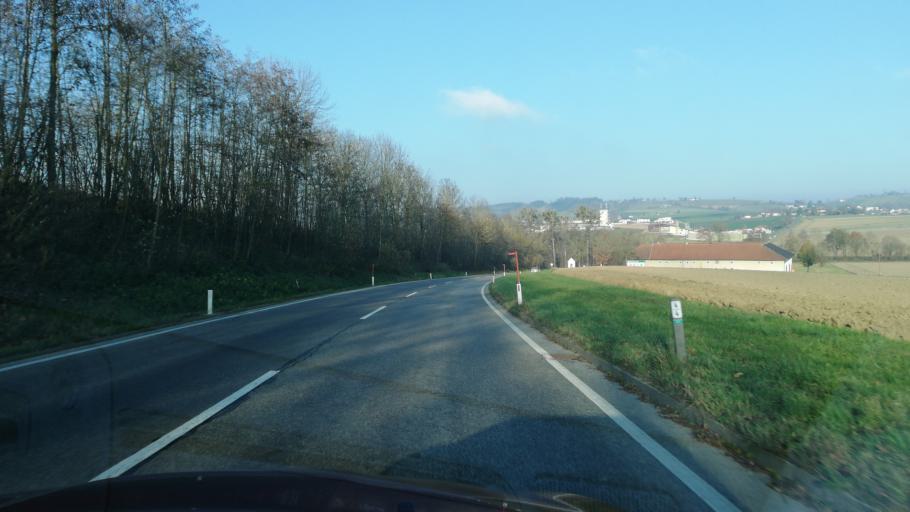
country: AT
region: Upper Austria
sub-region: Wels-Land
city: Buchkirchen
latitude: 48.2192
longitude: 14.0324
